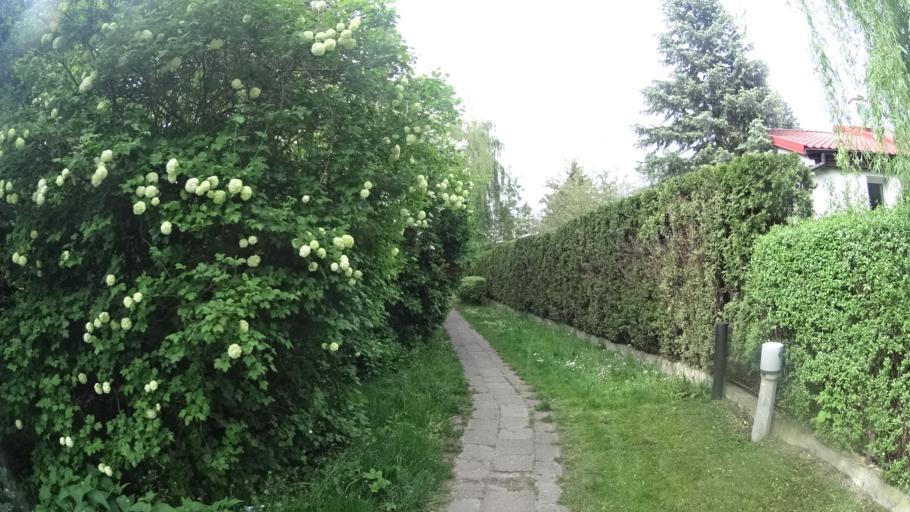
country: PL
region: Masovian Voivodeship
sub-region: Powiat warszawski zachodni
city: Babice
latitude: 52.2497
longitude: 20.8723
